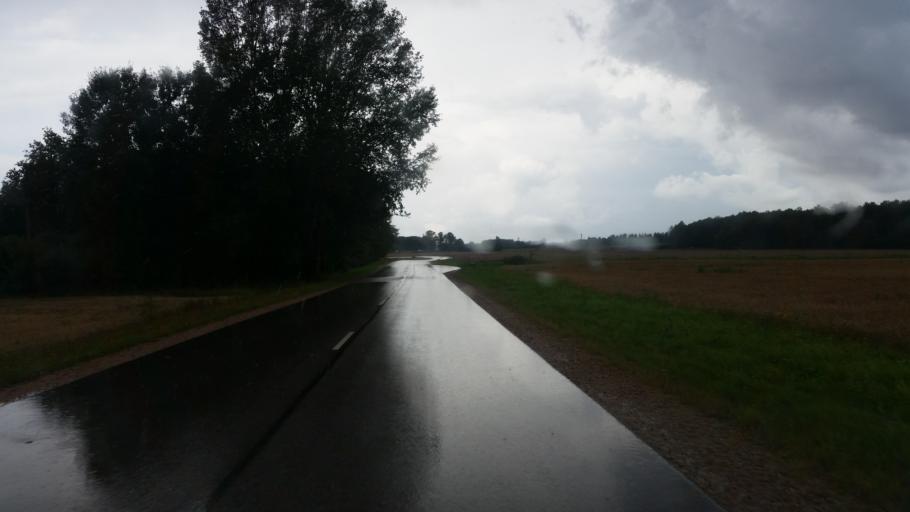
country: LV
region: Bauskas Rajons
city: Bauska
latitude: 56.4303
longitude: 24.3980
